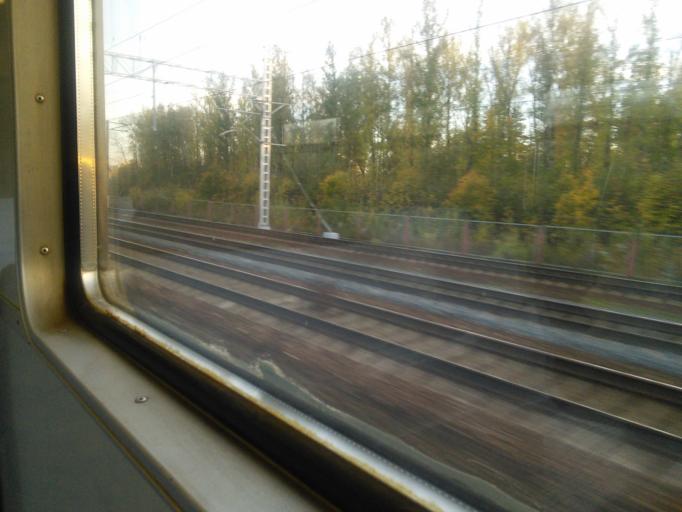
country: RU
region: Moskovskaya
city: Novopodrezkovo
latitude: 55.9316
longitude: 37.3635
